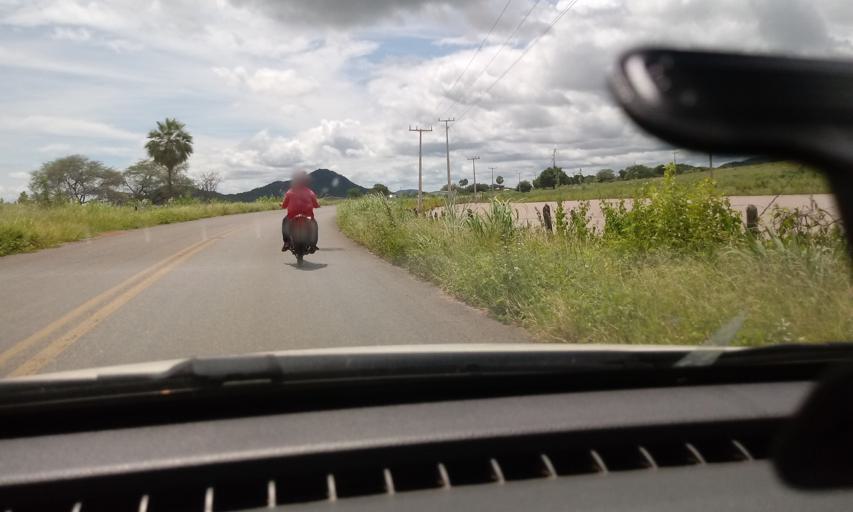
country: BR
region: Bahia
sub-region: Guanambi
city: Guanambi
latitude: -14.1397
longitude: -42.8461
